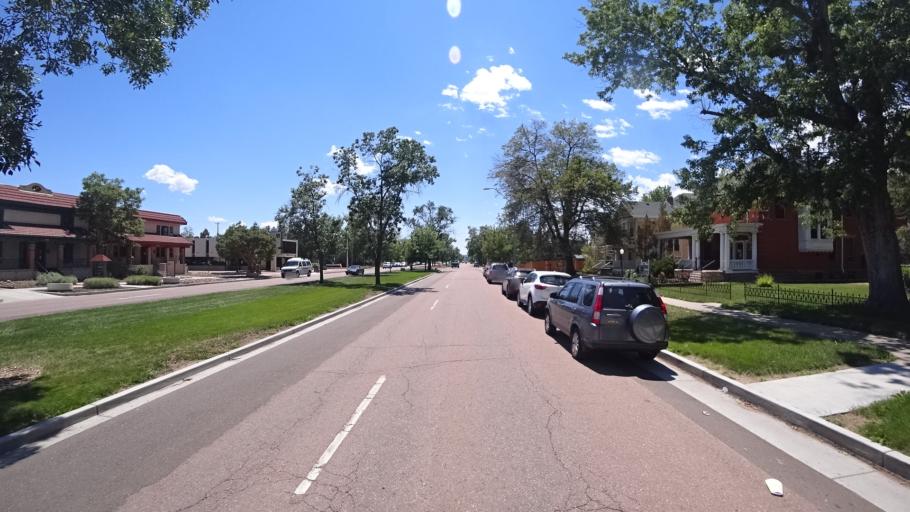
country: US
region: Colorado
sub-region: El Paso County
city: Colorado Springs
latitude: 38.8433
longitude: -104.8213
